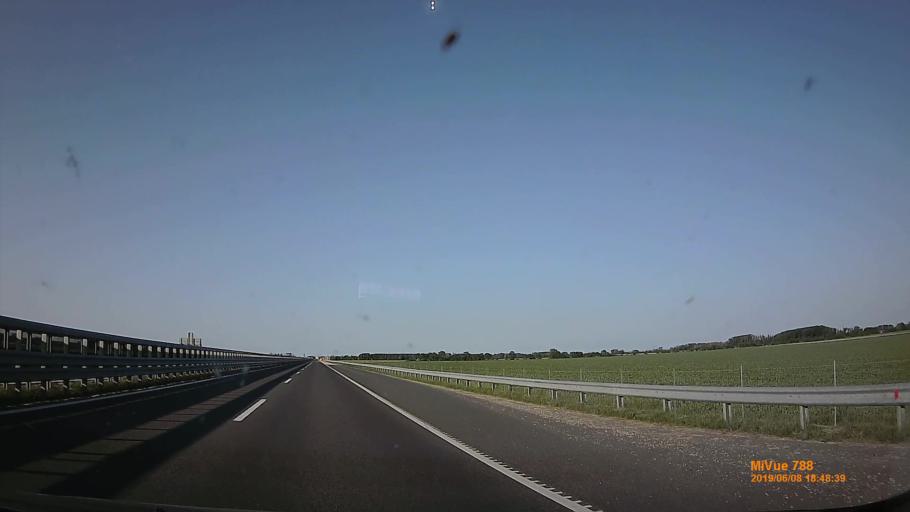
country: HU
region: Gyor-Moson-Sopron
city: Farad
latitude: 47.5206
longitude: 17.1941
